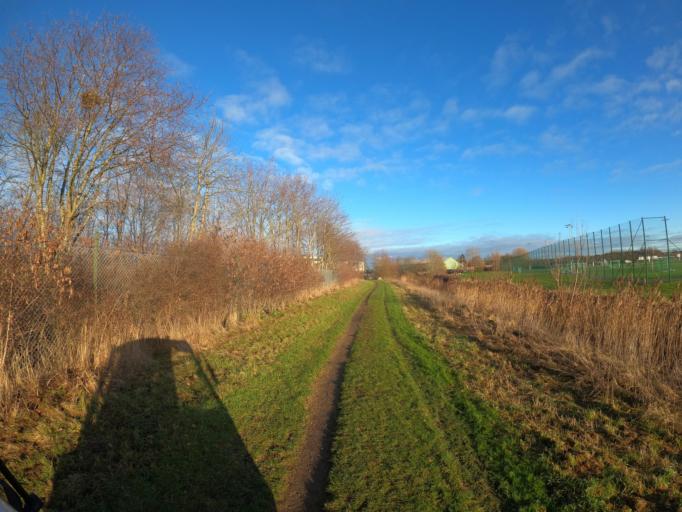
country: SE
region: Skane
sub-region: Svedala Kommun
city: Svedala
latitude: 55.5046
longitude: 13.2322
